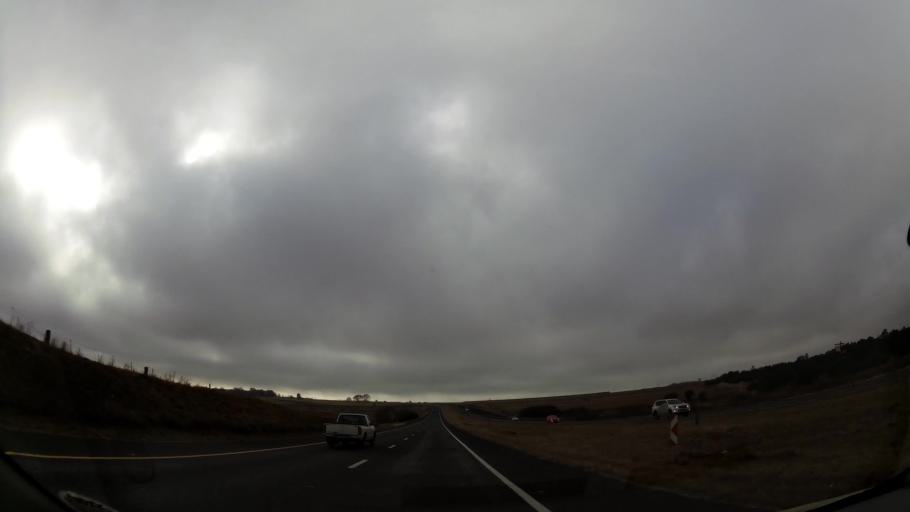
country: ZA
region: Mpumalanga
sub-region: Nkangala District Municipality
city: Delmas
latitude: -26.0677
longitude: 28.7805
